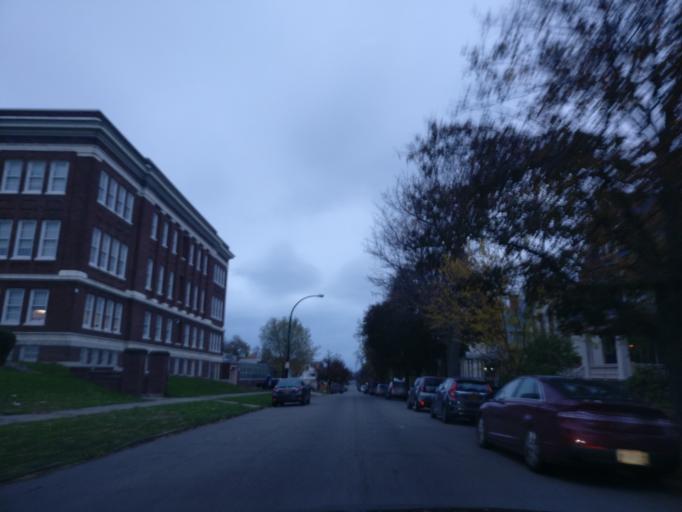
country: US
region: New York
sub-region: Erie County
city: Buffalo
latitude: 42.9036
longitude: -78.8842
